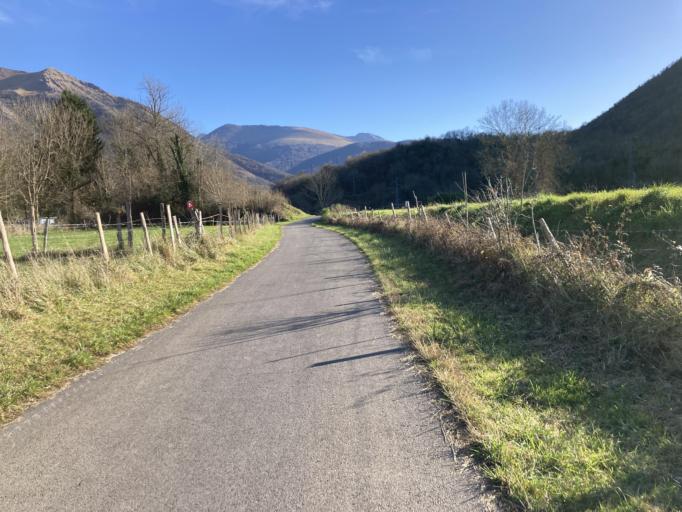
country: FR
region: Aquitaine
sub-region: Departement des Pyrenees-Atlantiques
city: Louvie-Juzon
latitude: 43.0923
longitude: -0.4318
